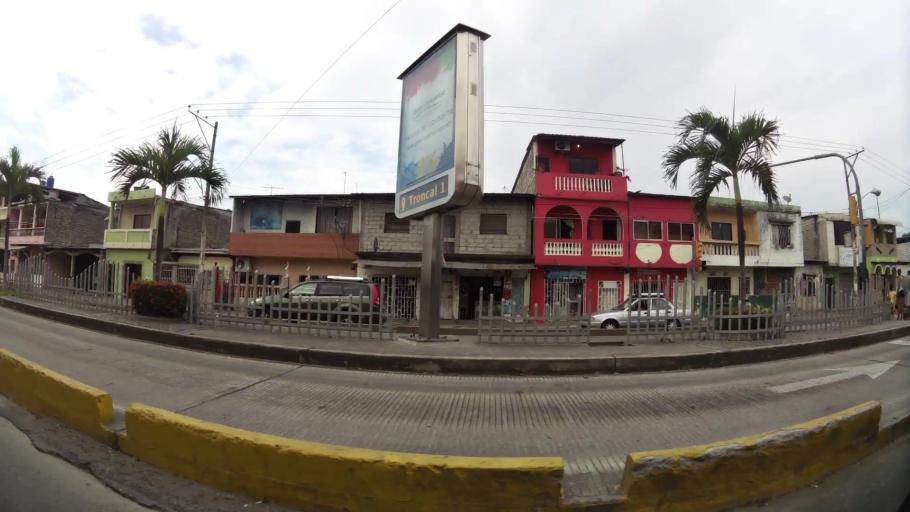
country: EC
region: Guayas
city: Guayaquil
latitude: -2.2601
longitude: -79.8788
